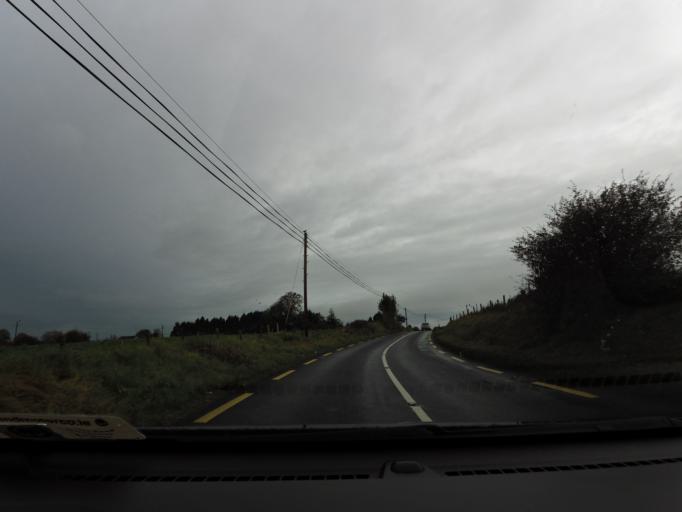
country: IE
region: Connaught
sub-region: County Galway
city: Tuam
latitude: 53.5487
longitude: -8.8091
